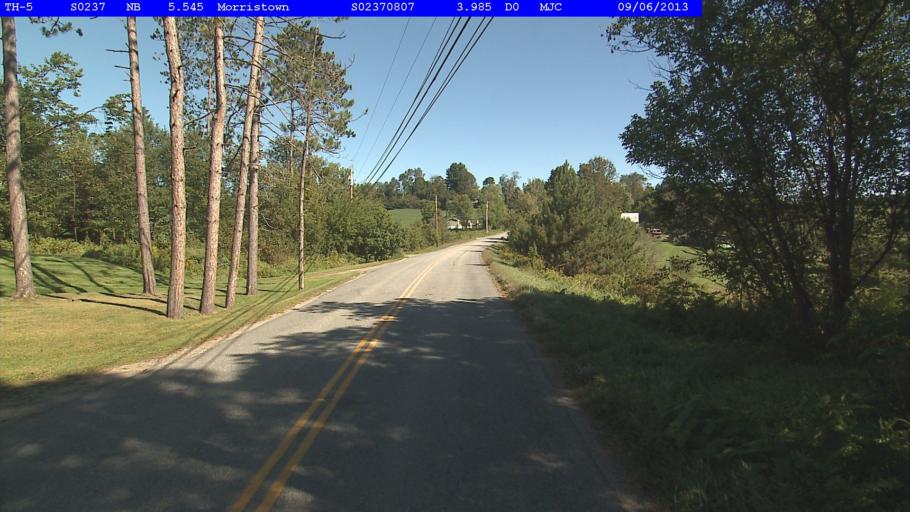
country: US
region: Vermont
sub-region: Lamoille County
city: Morristown
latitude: 44.5539
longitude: -72.6259
